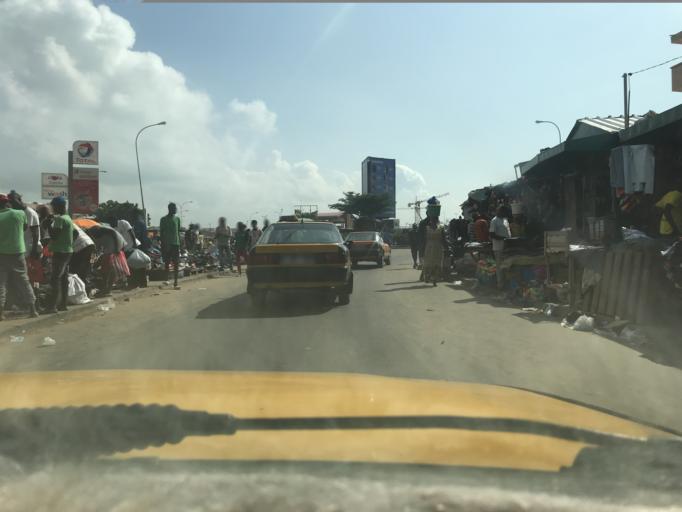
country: SN
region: Dakar
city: Dakar
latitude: 14.6978
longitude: -17.4446
